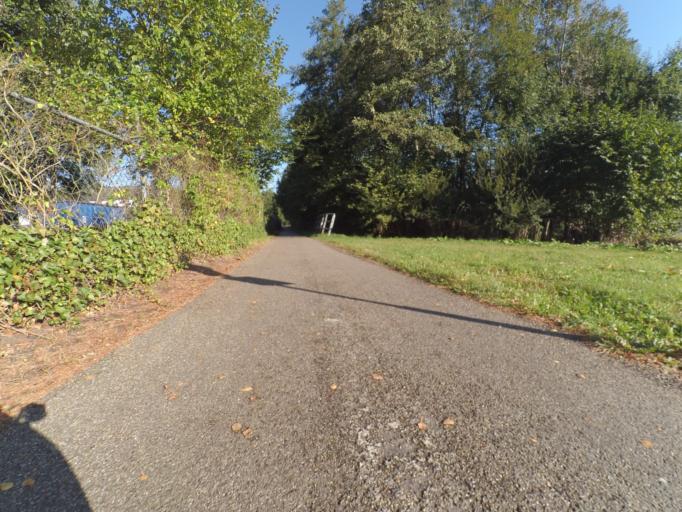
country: NL
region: Gelderland
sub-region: Gemeente Epe
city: Vaassen
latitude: 52.2556
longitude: 5.9663
